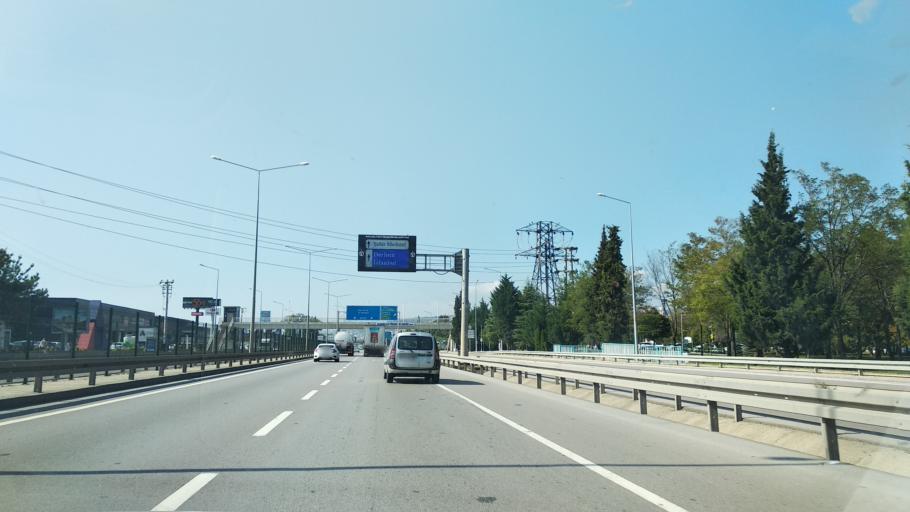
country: TR
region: Kocaeli
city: Kullar
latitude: 40.7602
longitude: 29.9771
